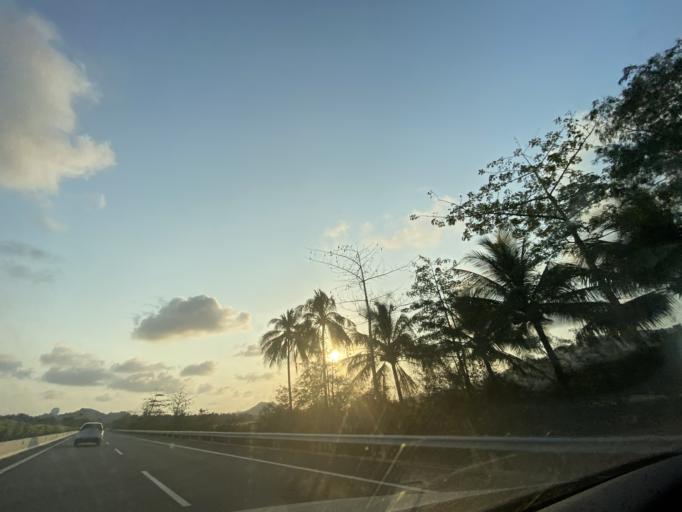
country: CN
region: Hainan
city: Longguang
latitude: 18.4572
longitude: 109.8896
